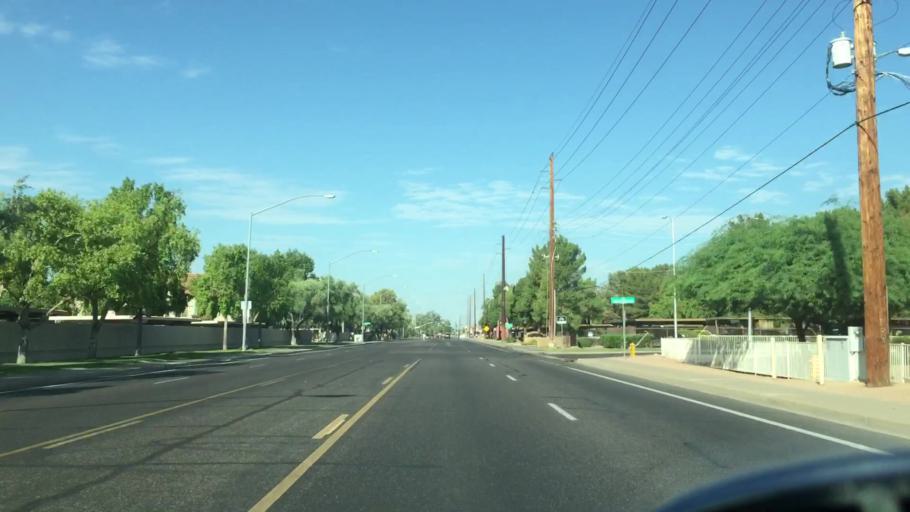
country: US
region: Arizona
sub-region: Maricopa County
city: Mesa
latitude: 33.4004
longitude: -111.8522
